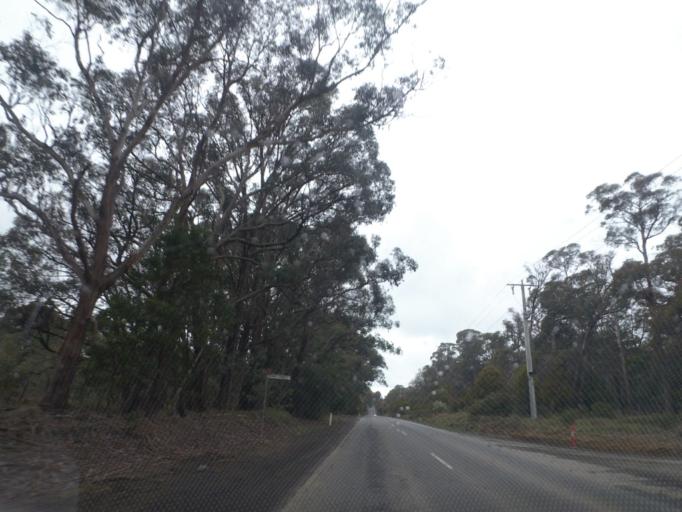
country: AU
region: Victoria
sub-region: Hume
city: Sunbury
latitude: -37.3452
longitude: 144.6732
